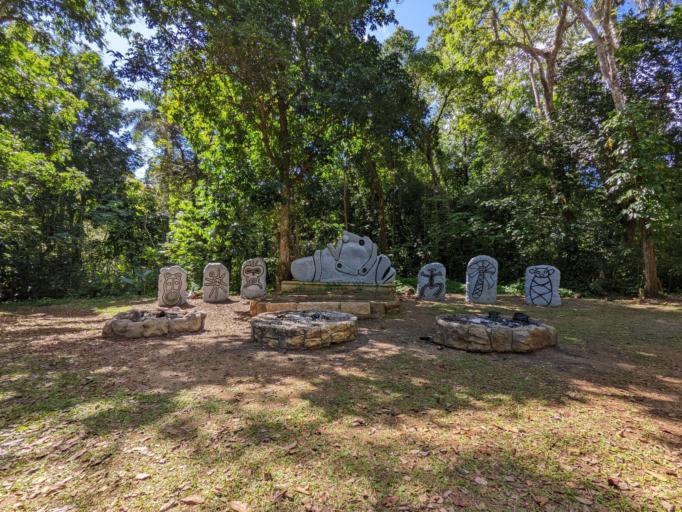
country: PR
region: San Sebastian
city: Juncal
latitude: 18.3696
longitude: -66.9189
